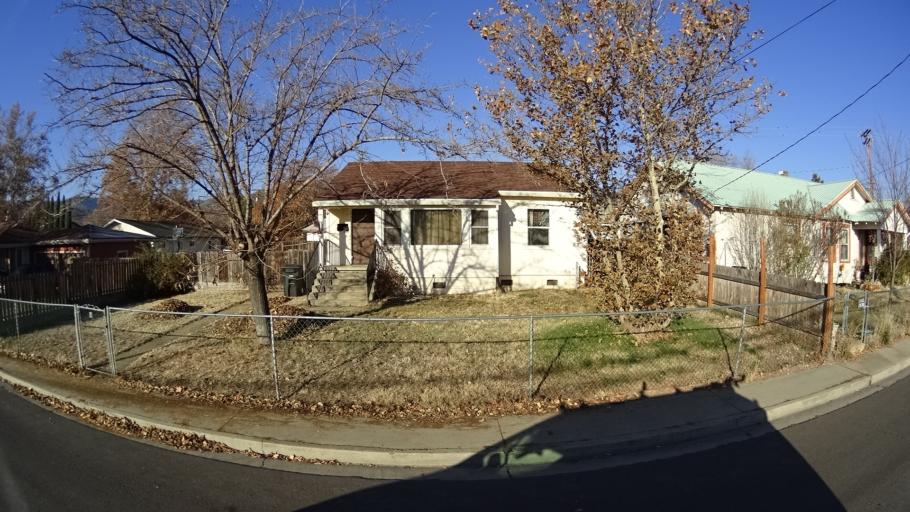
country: US
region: California
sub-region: Siskiyou County
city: Yreka
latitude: 41.7252
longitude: -122.6410
